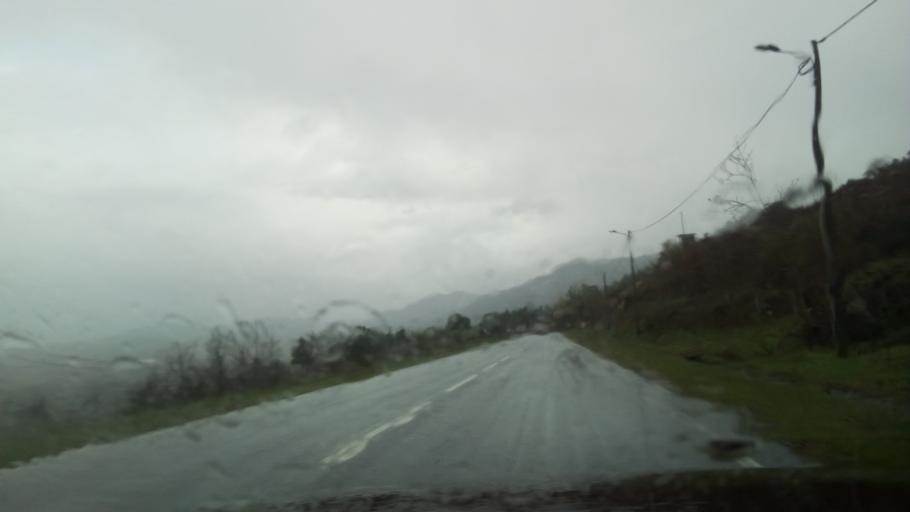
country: PT
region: Guarda
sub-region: Guarda
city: Guarda
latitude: 40.5762
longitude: -7.2963
